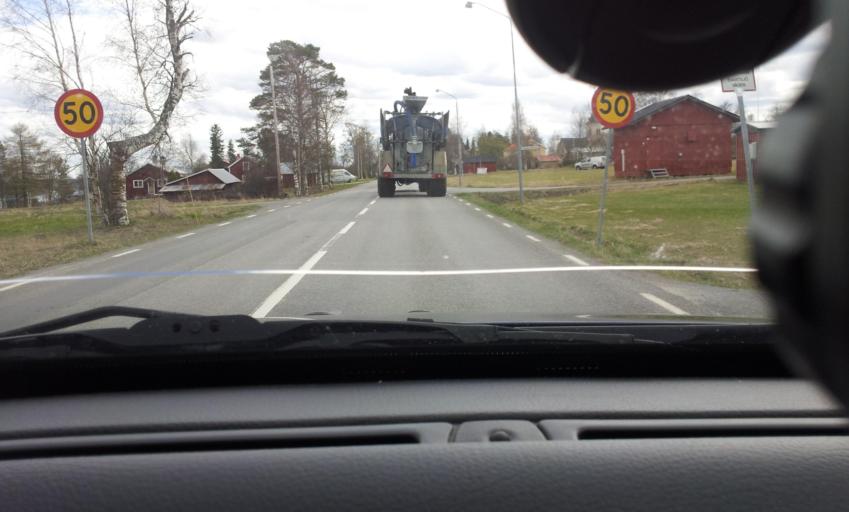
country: SE
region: Jaemtland
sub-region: OEstersunds Kommun
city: Brunflo
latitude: 63.1132
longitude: 14.7295
